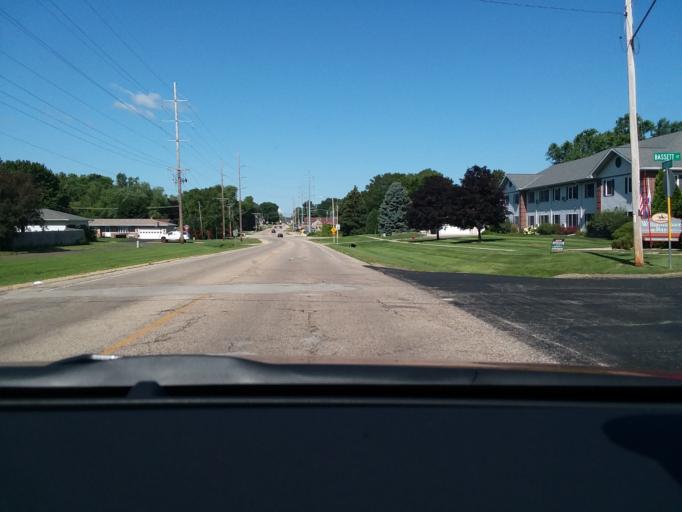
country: US
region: Wisconsin
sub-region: Dane County
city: De Forest
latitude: 43.2529
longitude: -89.3362
